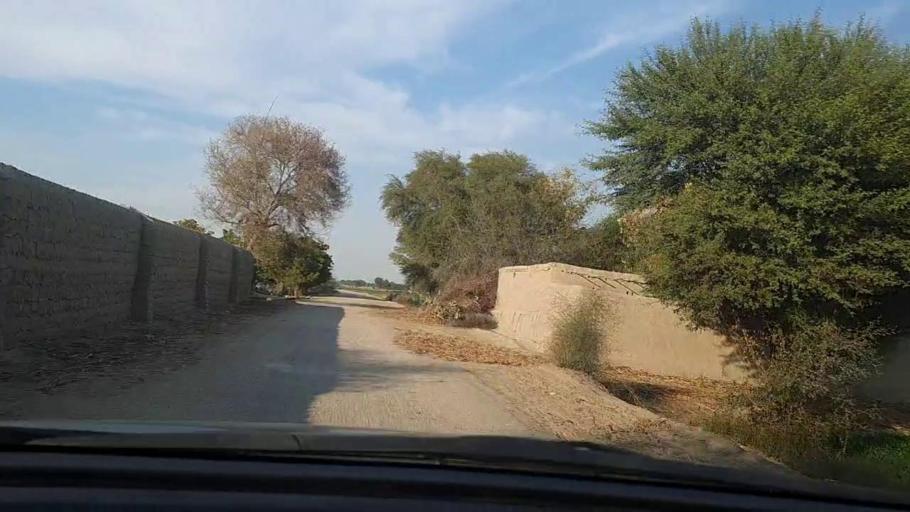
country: PK
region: Sindh
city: Daulatpur
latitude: 26.3232
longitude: 68.0266
